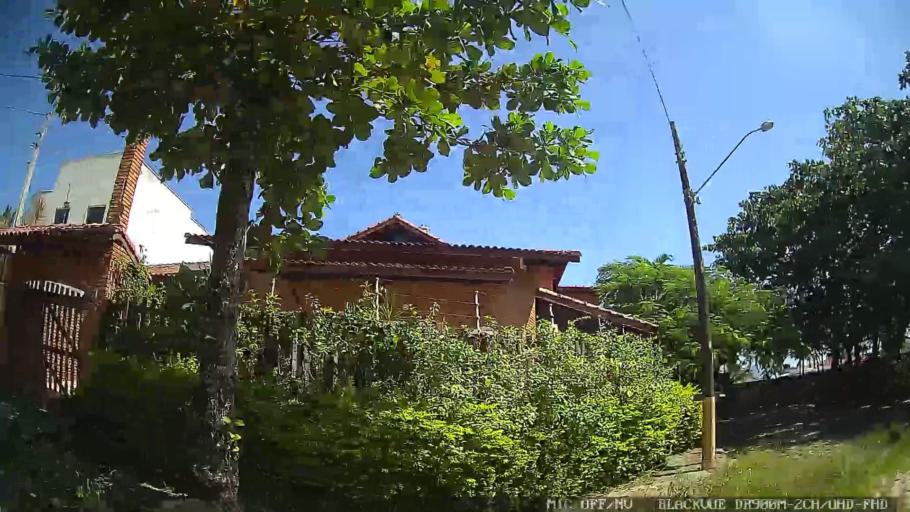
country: BR
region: Sao Paulo
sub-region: Peruibe
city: Peruibe
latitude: -24.3012
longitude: -46.9705
